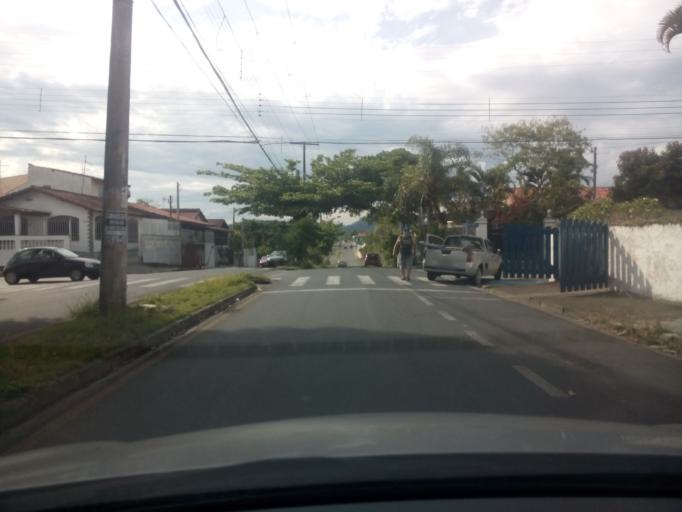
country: BR
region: Sao Paulo
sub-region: Peruibe
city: Peruibe
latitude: -24.3190
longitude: -46.9993
